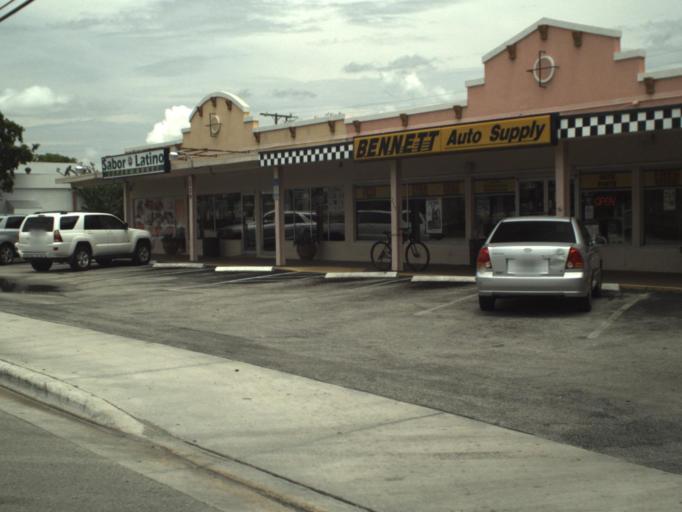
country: US
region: Florida
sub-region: Palm Beach County
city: Jupiter
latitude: 26.9342
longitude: -80.0966
